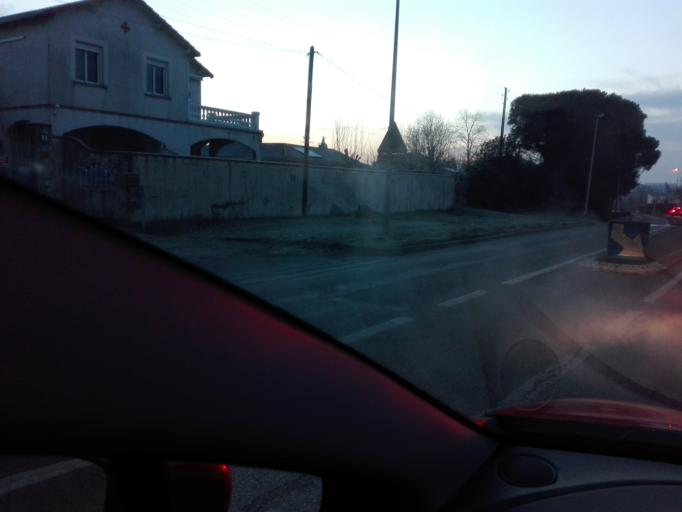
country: FR
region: Midi-Pyrenees
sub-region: Departement de la Haute-Garonne
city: Seilh
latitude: 43.6964
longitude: 1.3501
